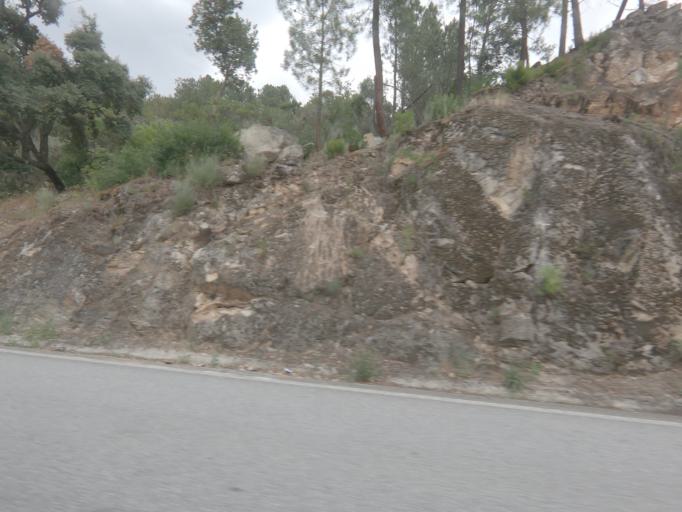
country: PT
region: Viseu
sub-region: Armamar
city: Armamar
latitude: 41.1137
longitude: -7.6743
